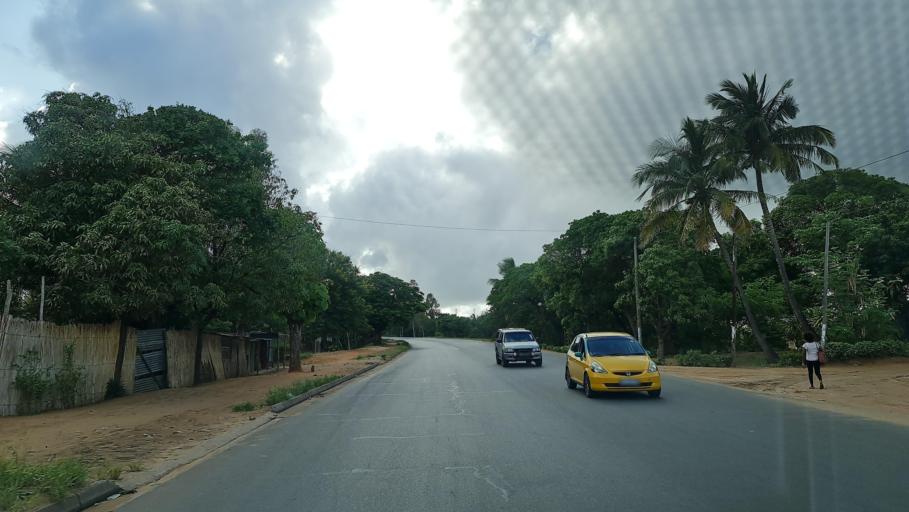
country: MZ
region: Gaza
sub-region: Xai-Xai District
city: Xai-Xai
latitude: -25.0572
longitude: 33.6775
